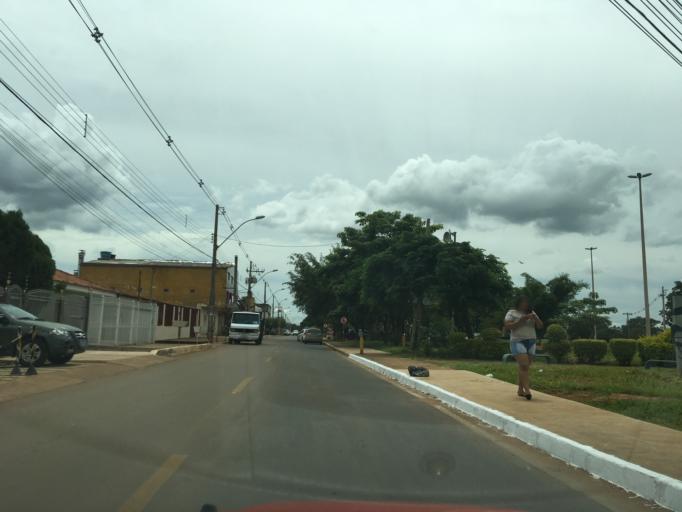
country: BR
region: Federal District
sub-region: Brasilia
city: Brasilia
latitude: -15.7961
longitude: -47.8532
